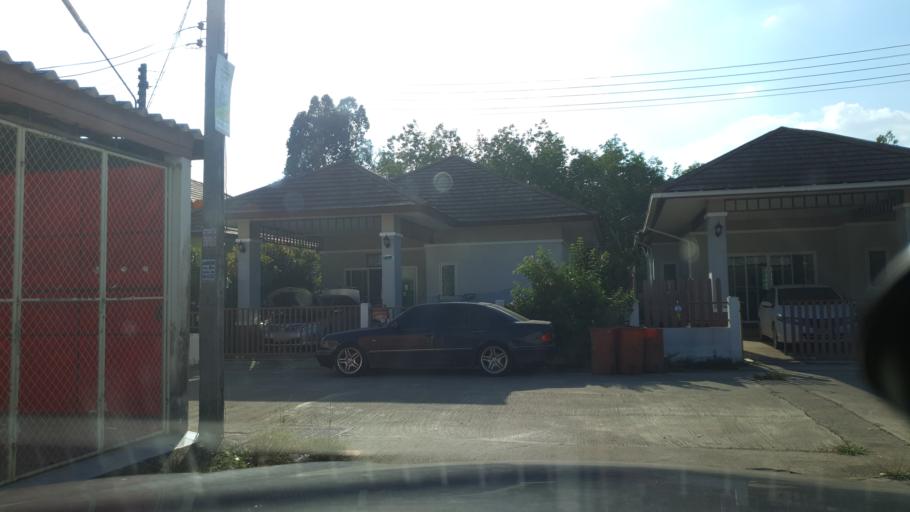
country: TH
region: Krabi
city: Nuea Khlong
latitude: 8.0832
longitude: 98.9881
